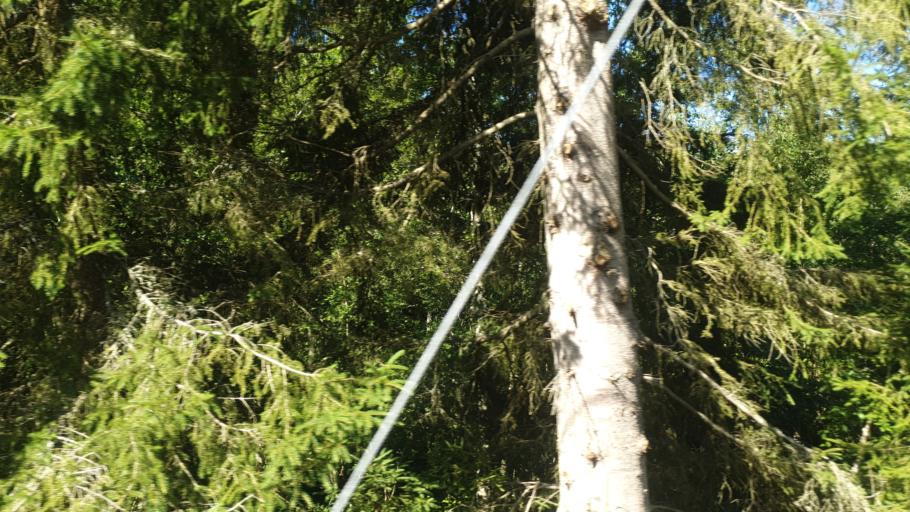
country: NO
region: Sor-Trondelag
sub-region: Meldal
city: Meldal
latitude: 63.1747
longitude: 9.7507
